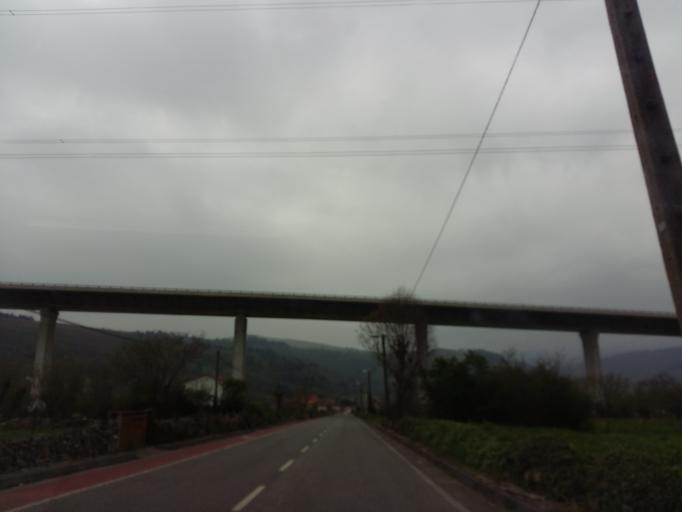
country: ES
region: Cantabria
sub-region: Provincia de Cantabria
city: Arenas de Iguna
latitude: 43.1928
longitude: -4.0720
